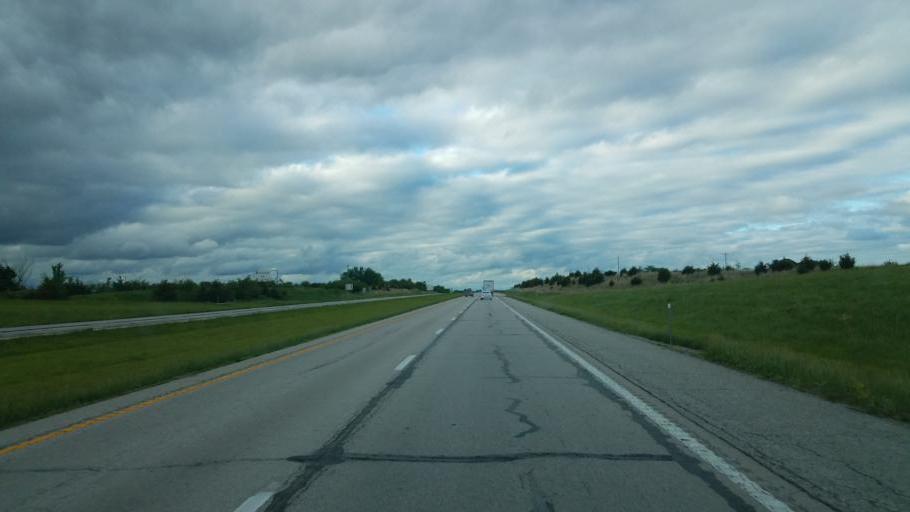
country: US
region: Missouri
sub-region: Harrison County
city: Bethany
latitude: 40.3750
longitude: -94.0026
